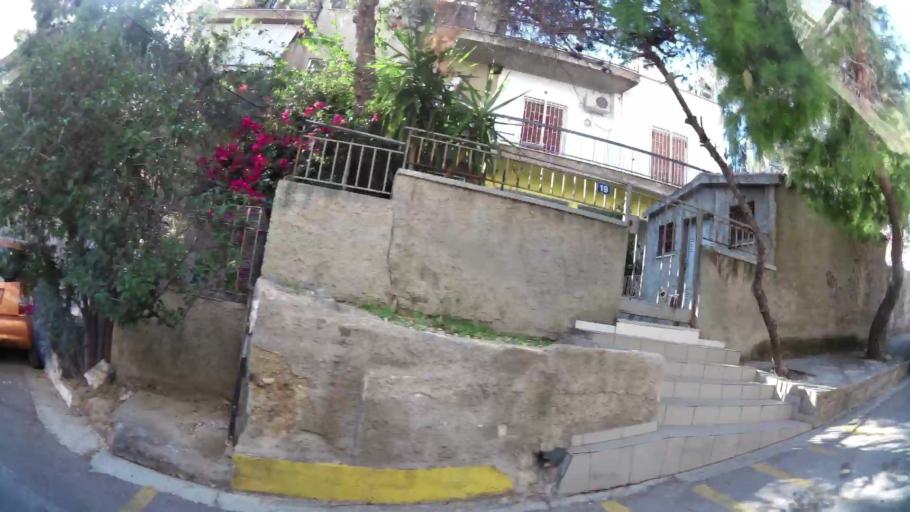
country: GR
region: Attica
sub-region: Nomos Piraios
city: Keratsini
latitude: 37.9657
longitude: 23.6321
